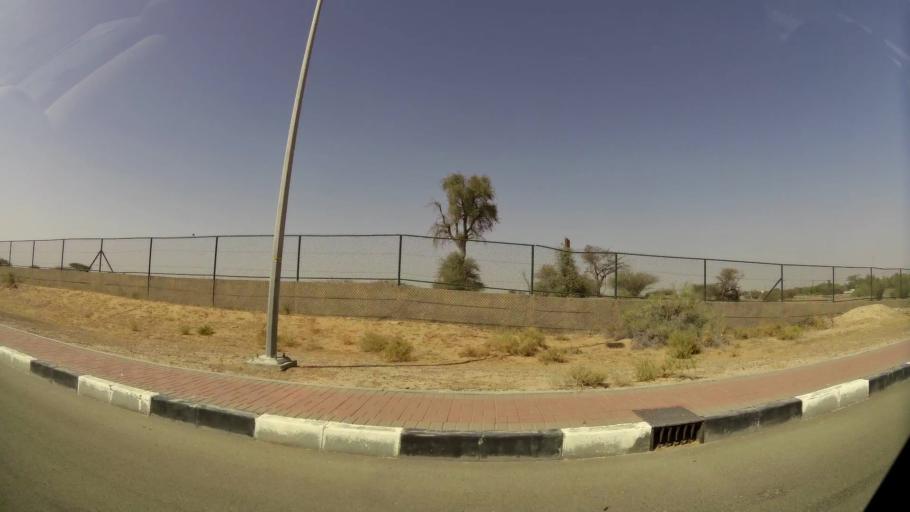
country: OM
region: Al Buraimi
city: Al Buraymi
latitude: 24.3007
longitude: 55.7925
